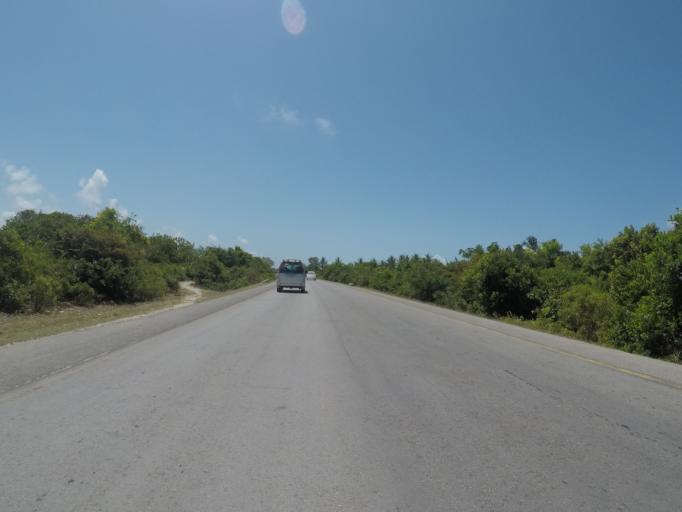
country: TZ
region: Zanzibar Central/South
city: Nganane
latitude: -6.3130
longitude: 39.5418
